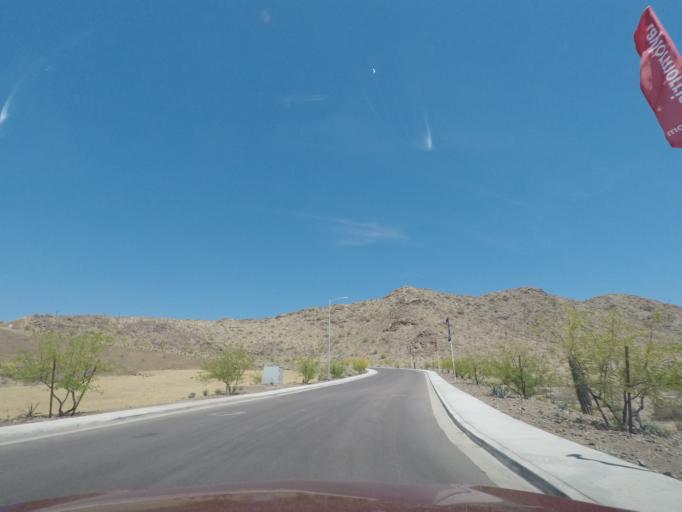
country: US
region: Arizona
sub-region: Maricopa County
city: Laveen
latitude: 33.2944
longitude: -112.1323
